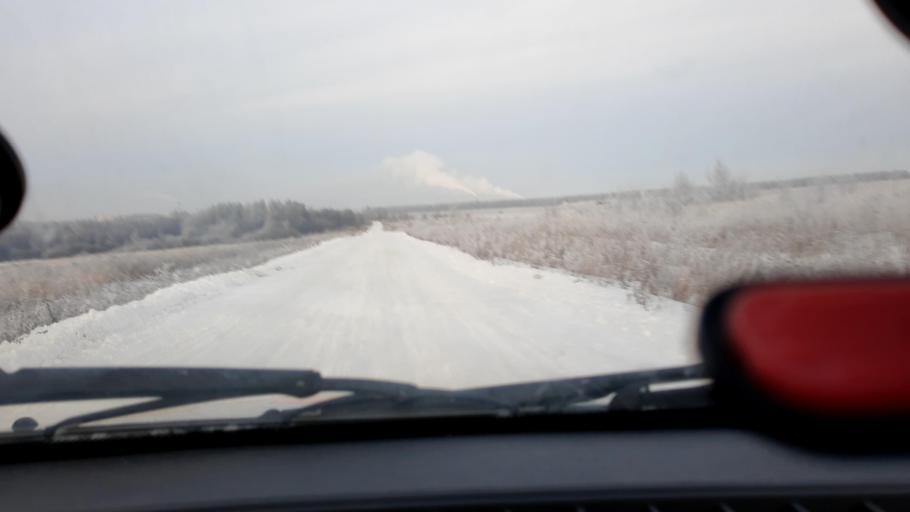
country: RU
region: Bashkortostan
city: Iglino
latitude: 54.7335
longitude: 56.2395
